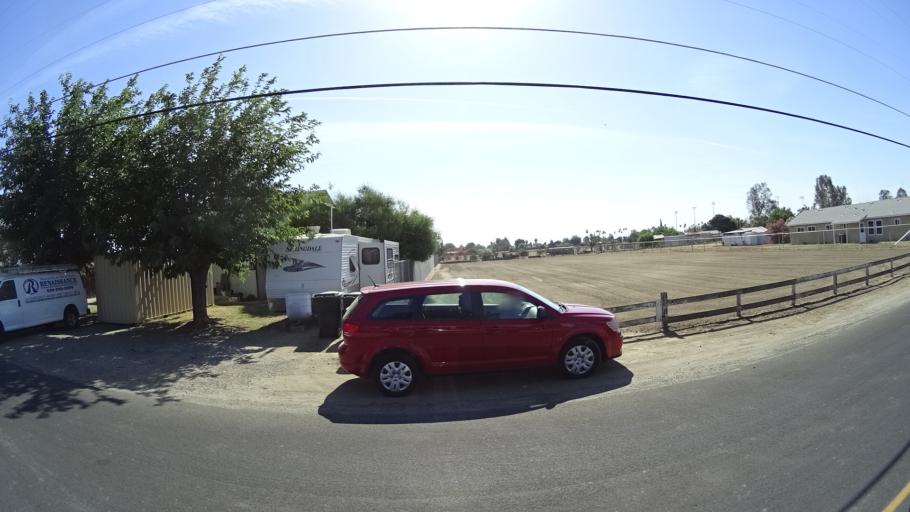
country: US
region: California
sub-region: Kings County
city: Hanford
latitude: 36.3415
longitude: -119.6325
